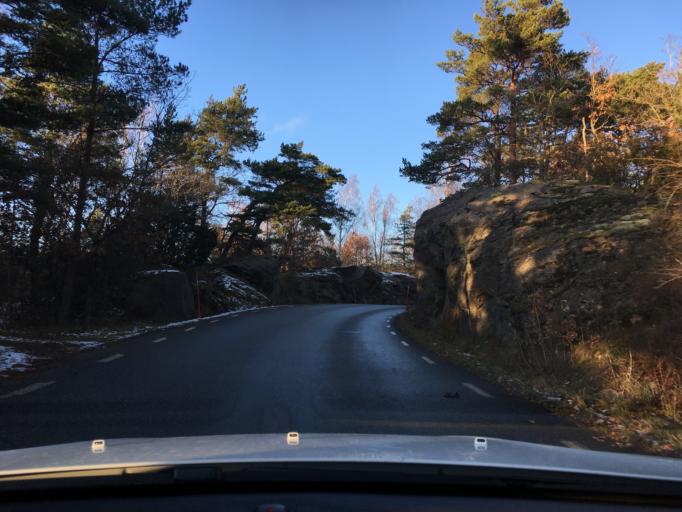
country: SE
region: Vaestra Goetaland
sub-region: Tjorns Kommun
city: Myggenas
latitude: 58.0609
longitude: 11.6819
